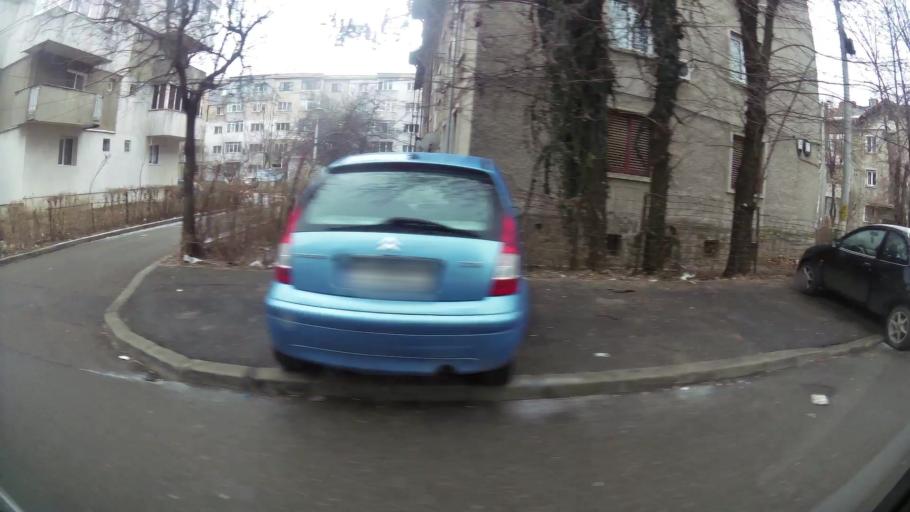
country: RO
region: Prahova
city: Ploiesti
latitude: 44.9392
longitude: 26.0456
